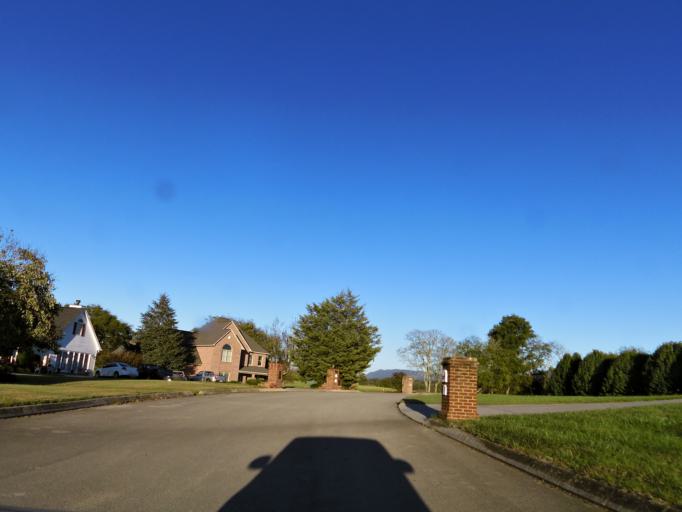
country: US
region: Tennessee
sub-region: Blount County
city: Wildwood
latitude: 35.7754
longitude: -83.8458
